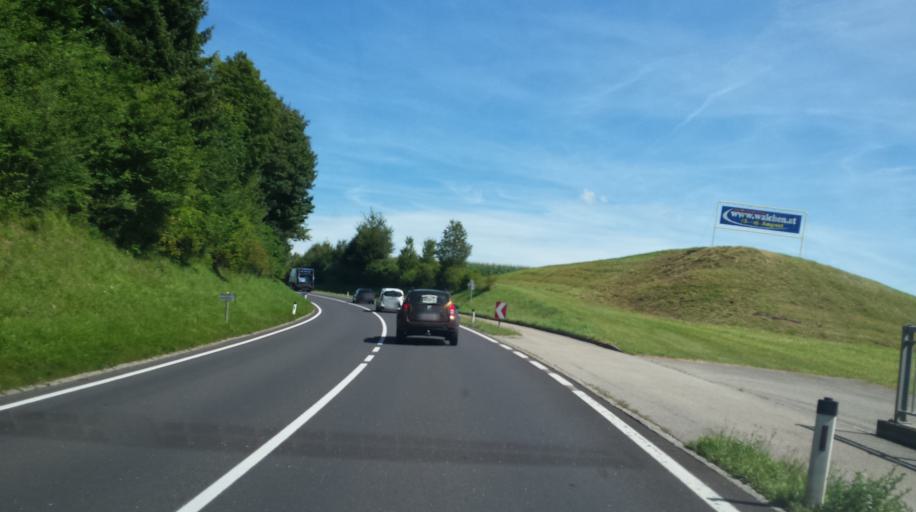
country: AT
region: Upper Austria
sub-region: Politischer Bezirk Vocklabruck
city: Frankenmarkt
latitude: 47.9855
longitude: 13.4041
